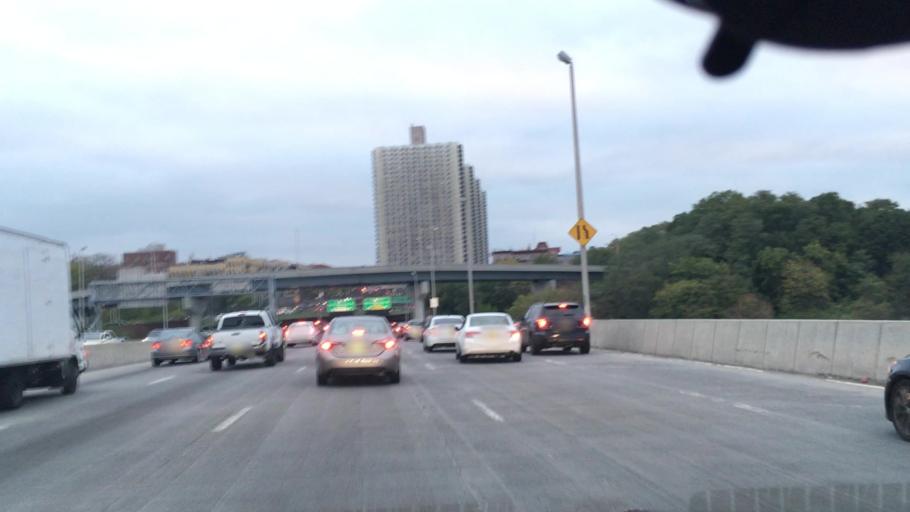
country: US
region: New York
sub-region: New York County
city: Inwood
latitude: 40.8455
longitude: -73.9280
